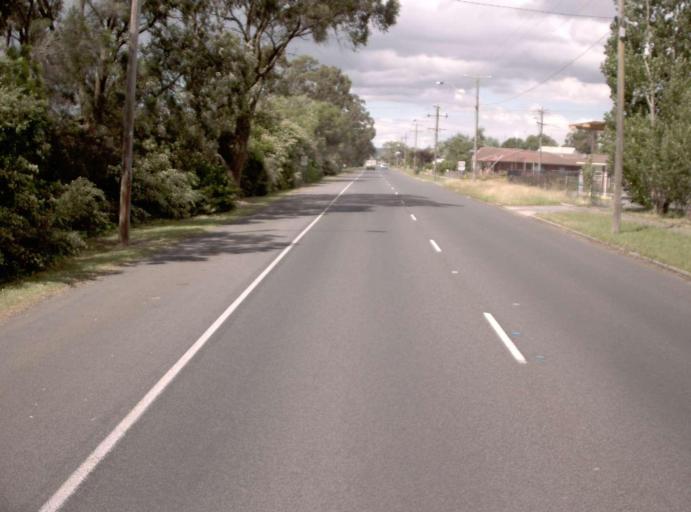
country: AU
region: Victoria
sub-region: Latrobe
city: Moe
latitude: -38.1832
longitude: 146.2403
